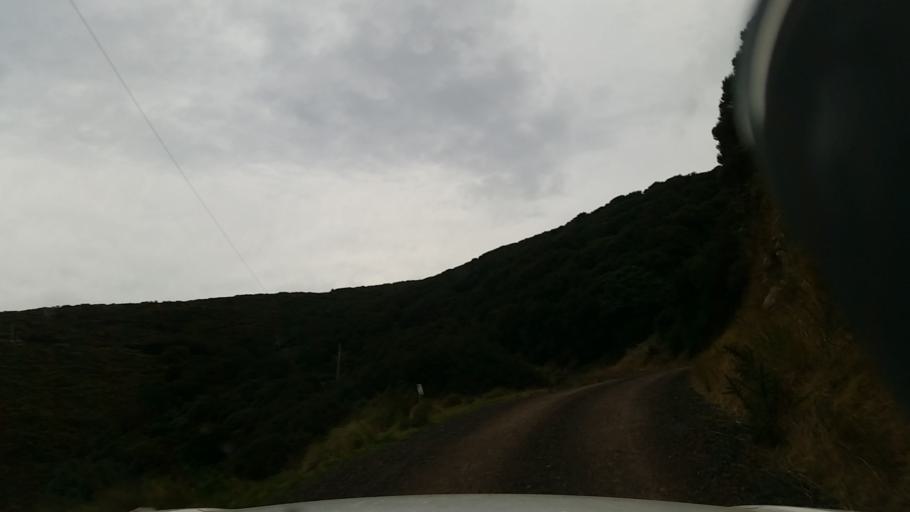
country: NZ
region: Canterbury
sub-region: Christchurch City
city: Christchurch
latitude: -43.8461
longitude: 172.9788
